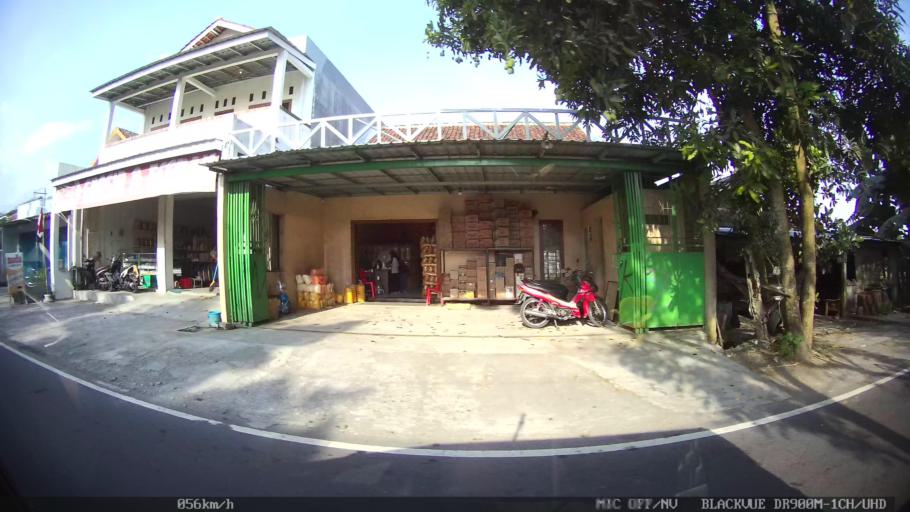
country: ID
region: Daerah Istimewa Yogyakarta
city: Bantul
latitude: -7.8806
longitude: 110.3195
